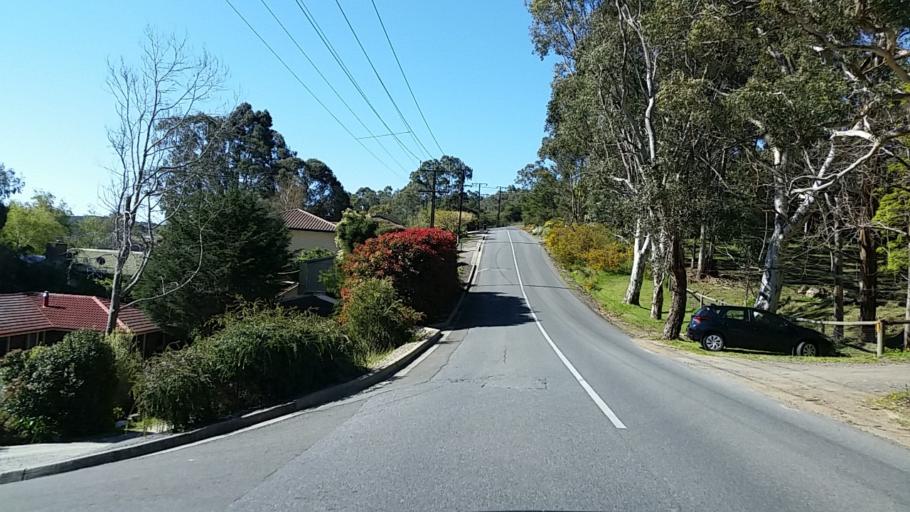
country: AU
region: South Australia
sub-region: Adelaide Hills
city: Lobethal
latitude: -34.9073
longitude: 138.8788
